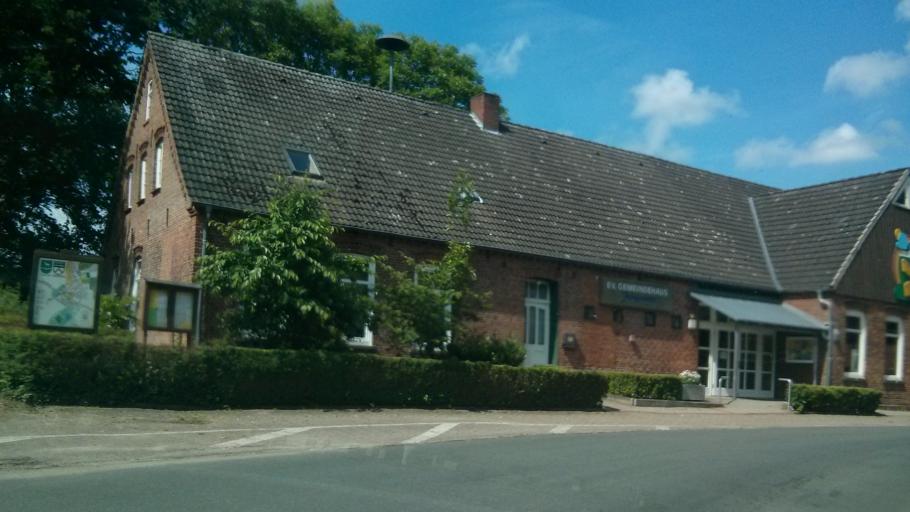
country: DE
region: Lower Saxony
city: Loxstedt
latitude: 53.4900
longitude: 8.6924
